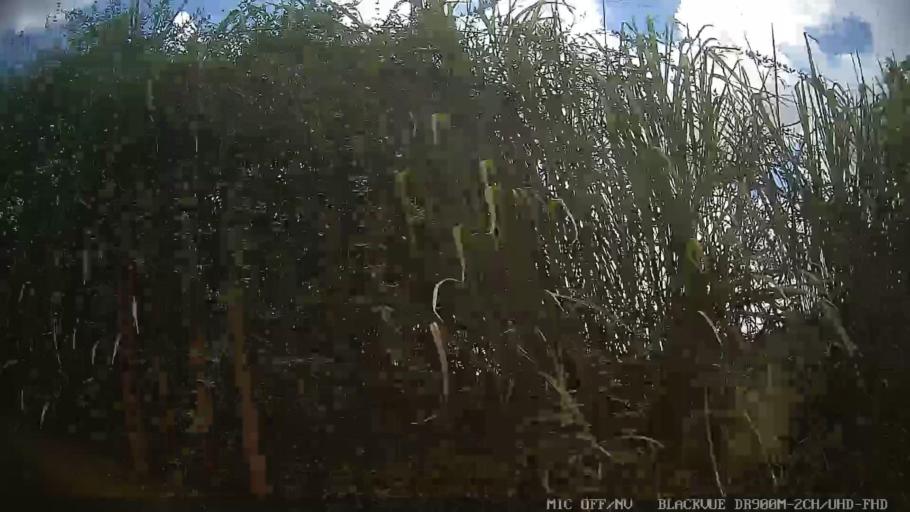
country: BR
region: Sao Paulo
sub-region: Atibaia
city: Atibaia
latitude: -23.1426
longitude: -46.6164
